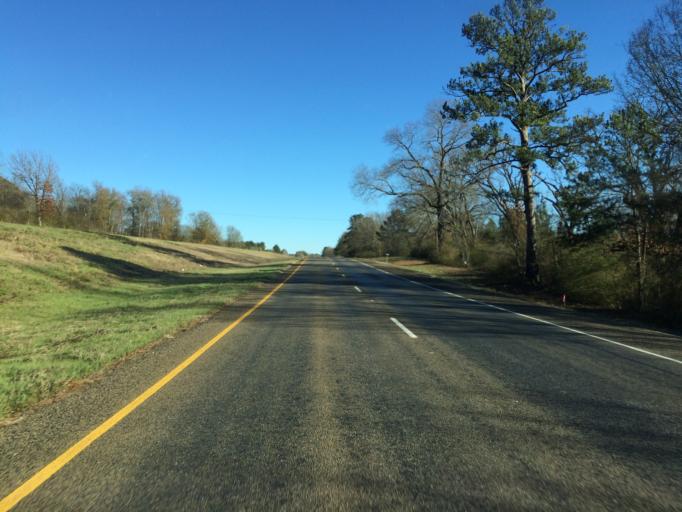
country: US
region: Texas
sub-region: Wood County
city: Hawkins
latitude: 32.5926
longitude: -95.2293
